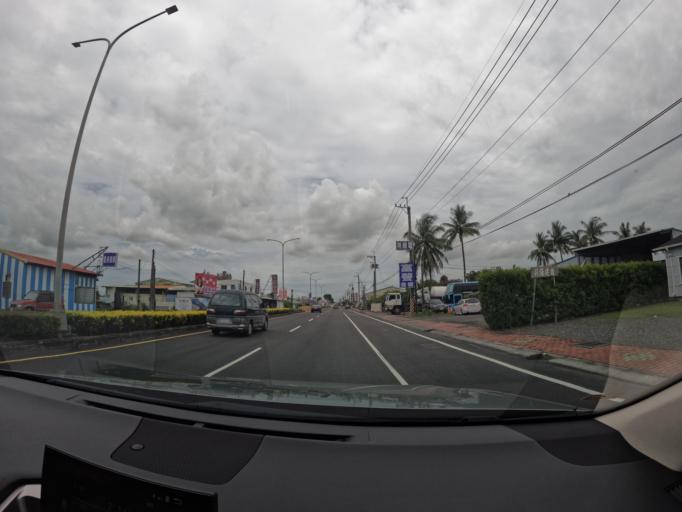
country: TW
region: Taiwan
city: Fengshan
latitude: 22.7860
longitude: 120.3107
